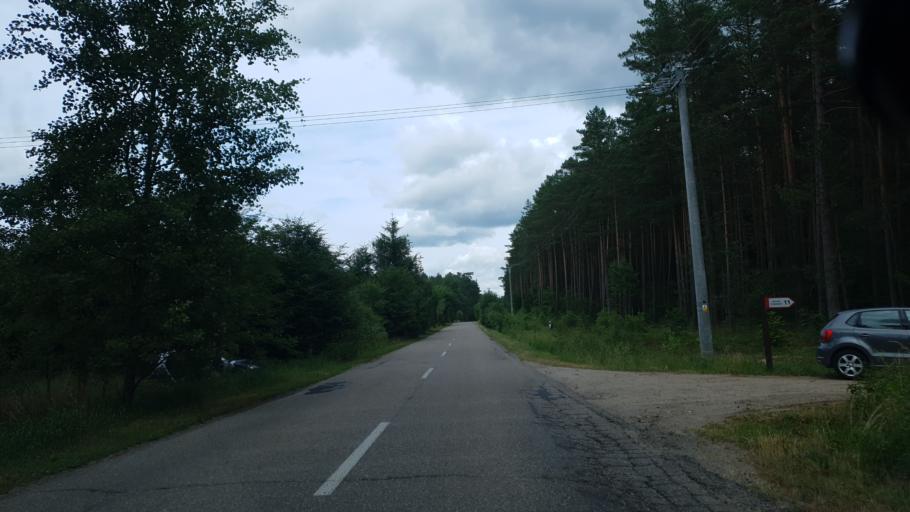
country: PL
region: Pomeranian Voivodeship
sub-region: Powiat kartuski
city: Stezyca
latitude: 54.2485
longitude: 18.0045
